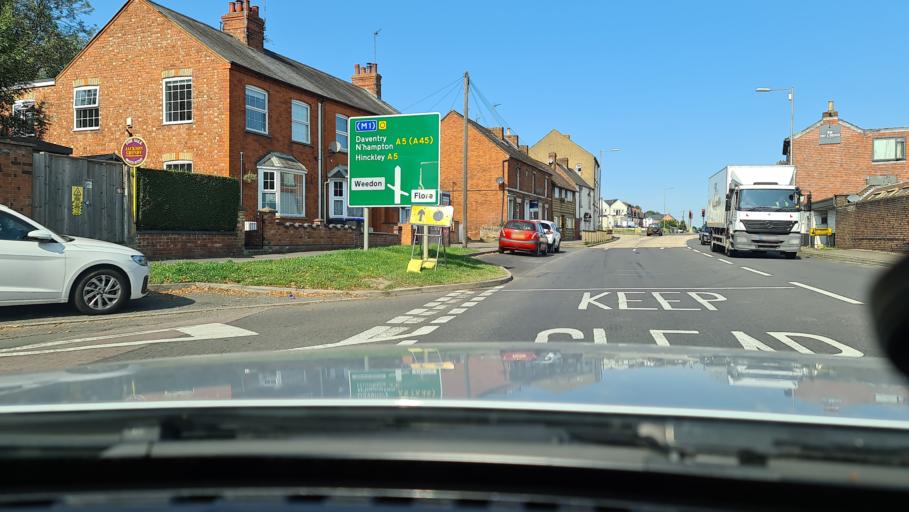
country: GB
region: England
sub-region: Northamptonshire
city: Bugbrooke
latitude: 52.2326
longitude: -1.0750
